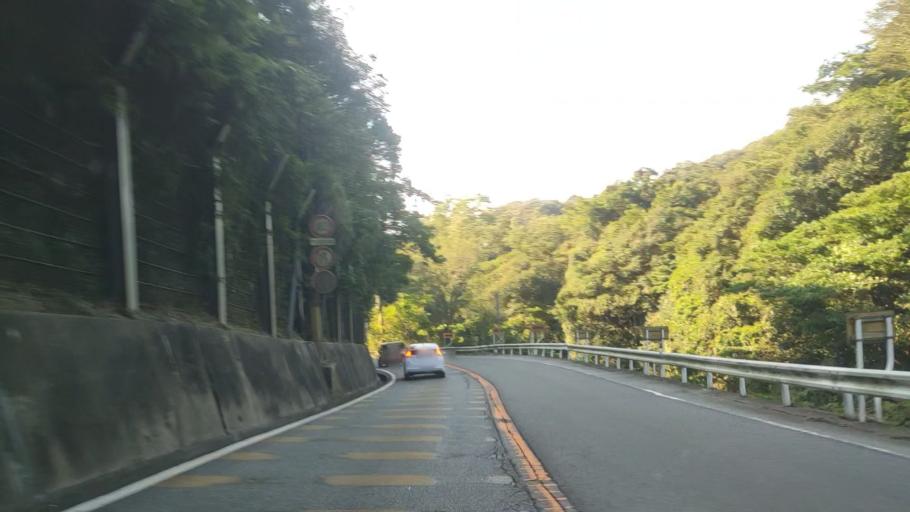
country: JP
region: Hyogo
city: Kobe
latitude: 34.7138
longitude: 135.1596
